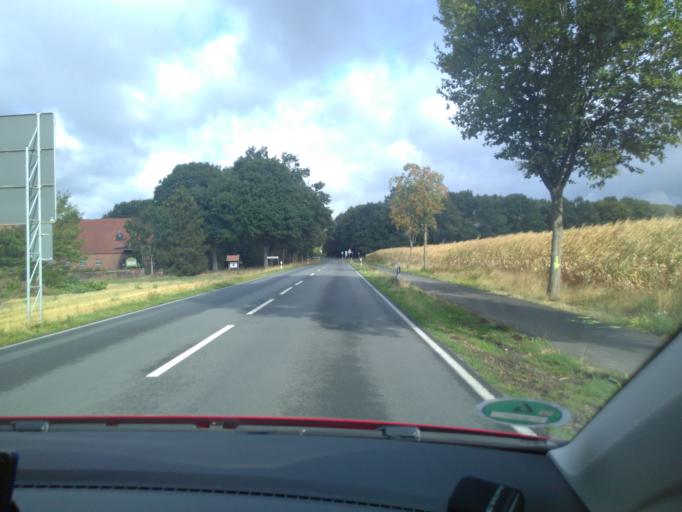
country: DE
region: North Rhine-Westphalia
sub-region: Regierungsbezirk Munster
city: Warendorf
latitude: 51.9644
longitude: 7.9781
